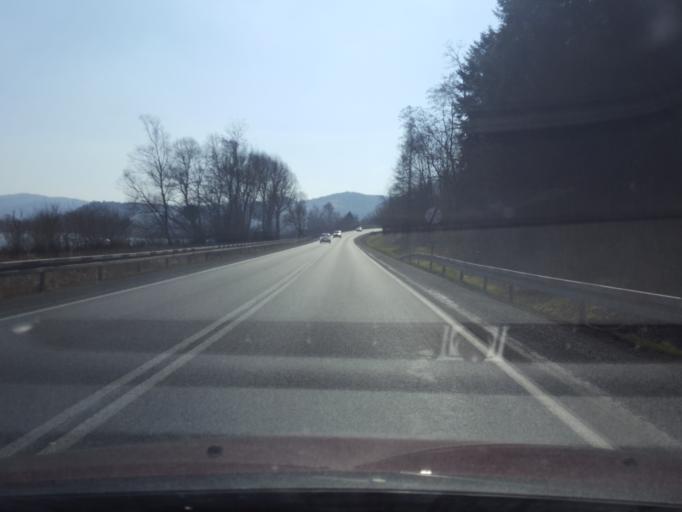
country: PL
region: Lesser Poland Voivodeship
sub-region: Powiat nowosadecki
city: Lososina Dolna
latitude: 49.7944
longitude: 20.6451
